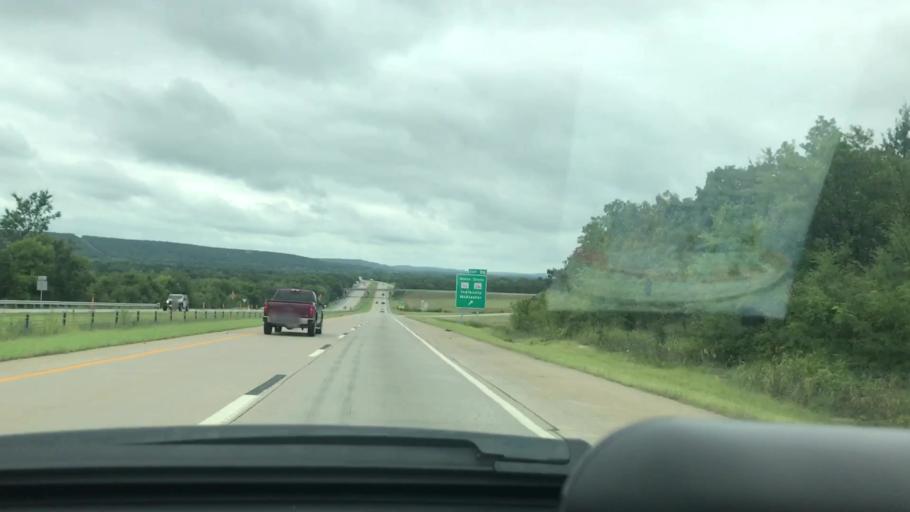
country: US
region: Oklahoma
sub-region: Pittsburg County
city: Krebs
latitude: 34.9938
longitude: -95.7213
